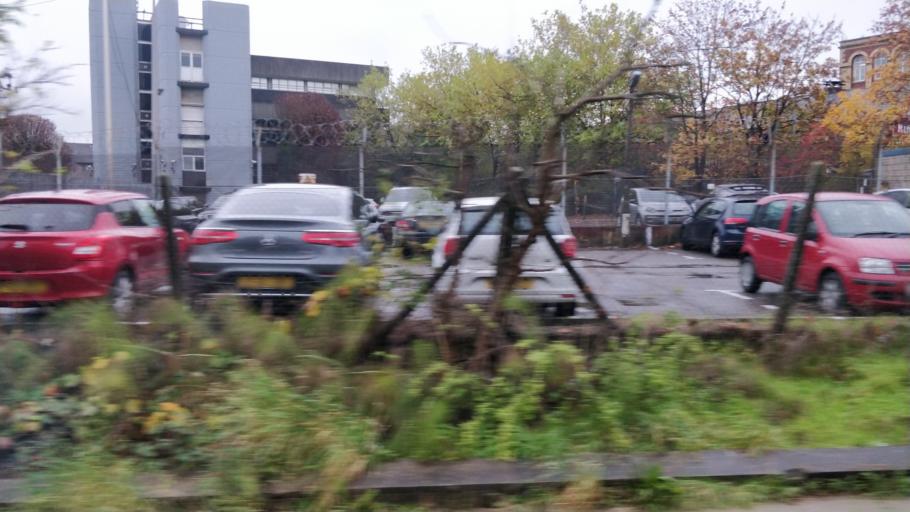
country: GB
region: England
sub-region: Borough of Wigan
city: Ince-in-Makerfield
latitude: 53.5457
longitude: -2.6370
